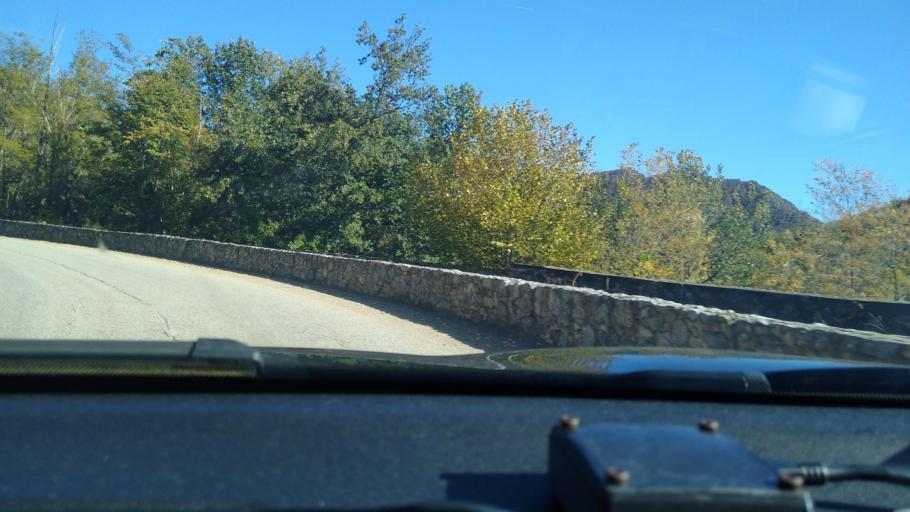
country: FR
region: Midi-Pyrenees
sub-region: Departement de l'Ariege
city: Ax-les-Thermes
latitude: 42.7223
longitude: 1.8512
